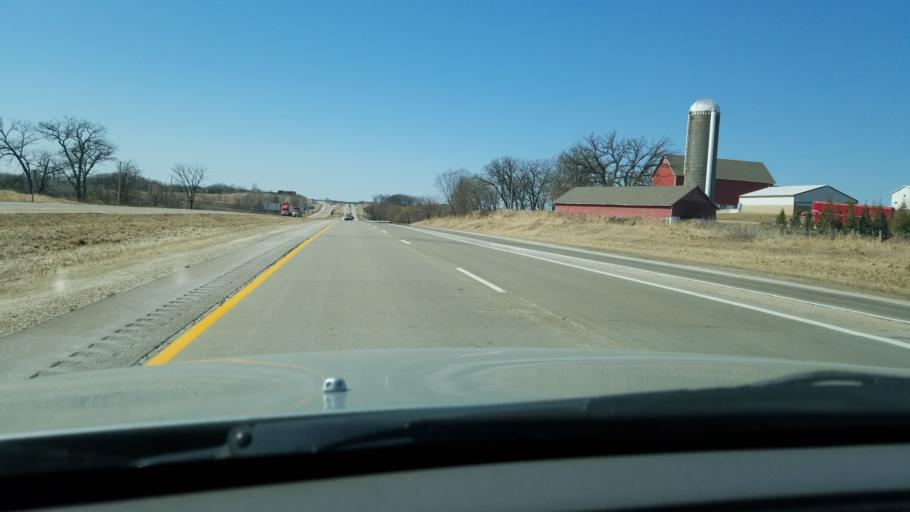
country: US
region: Wisconsin
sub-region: Dane County
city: Verona
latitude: 42.9867
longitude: -89.5646
